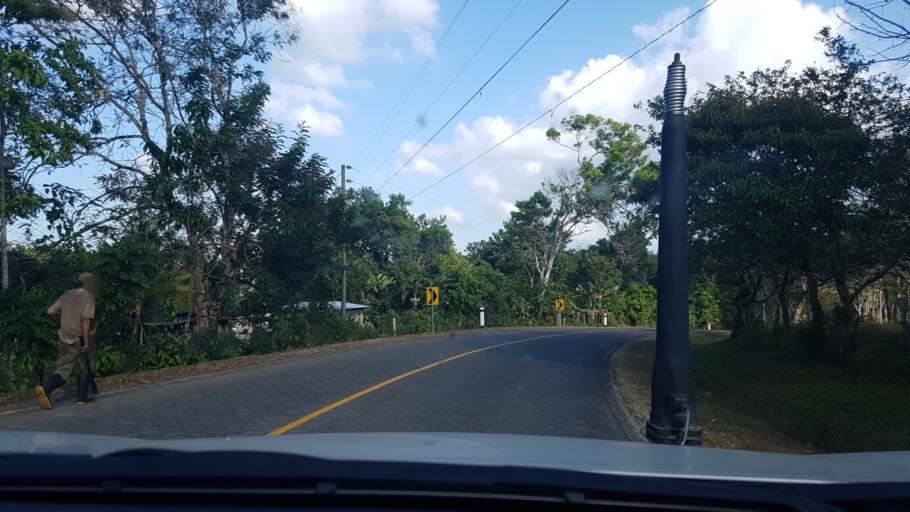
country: NI
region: Atlantico Sur
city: Nueva Guinea
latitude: 11.6962
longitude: -84.4077
